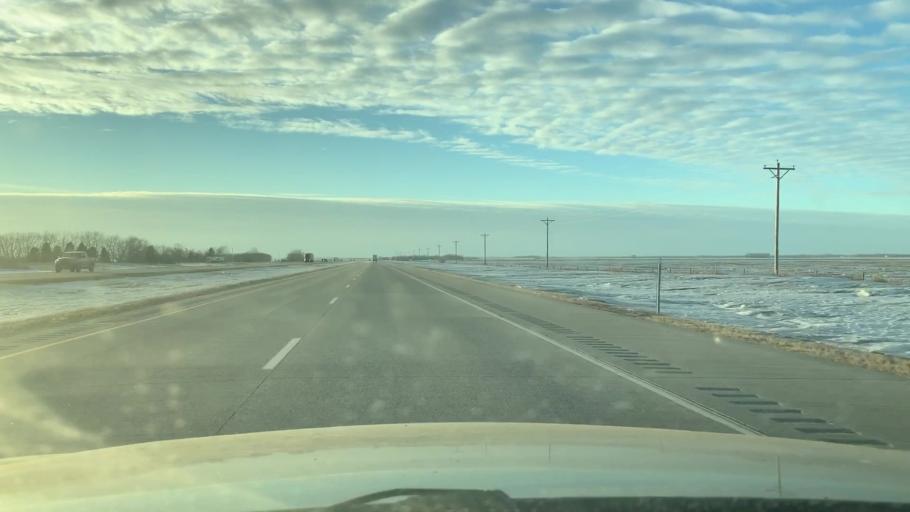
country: US
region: North Dakota
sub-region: Cass County
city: Casselton
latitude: 46.8760
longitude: -97.2902
